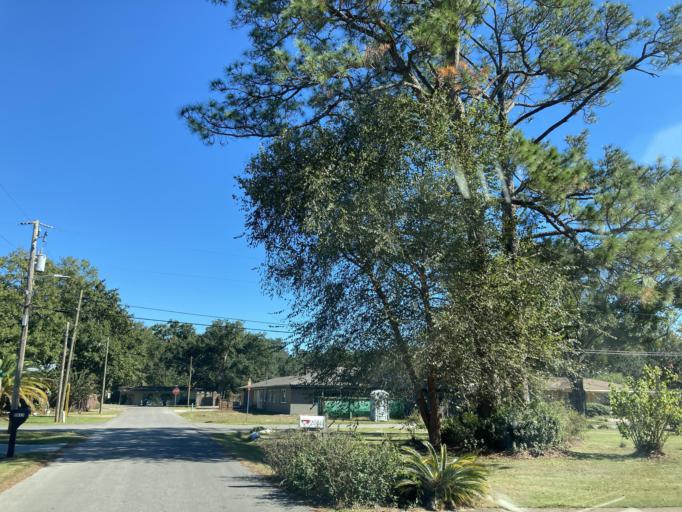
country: US
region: Mississippi
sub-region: Jackson County
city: Ocean Springs
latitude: 30.4093
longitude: -88.8132
